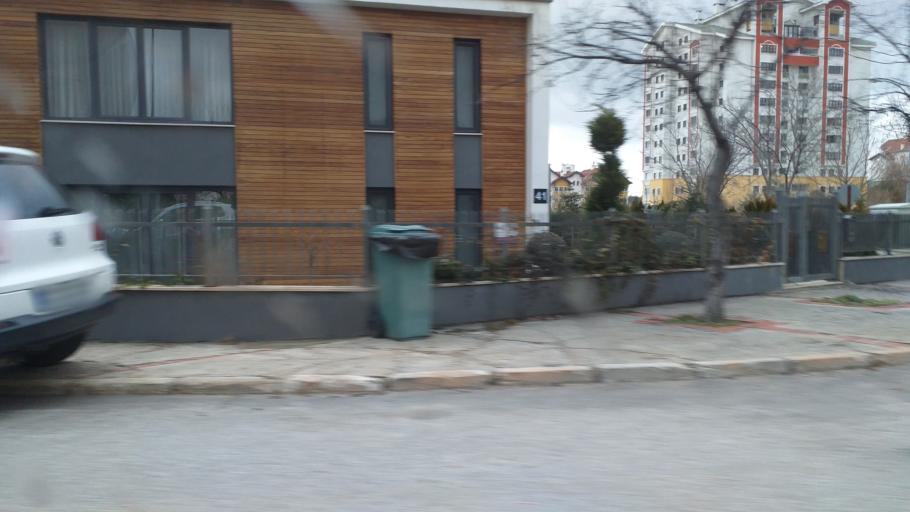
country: TR
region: Ankara
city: Batikent
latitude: 39.8756
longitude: 32.7150
